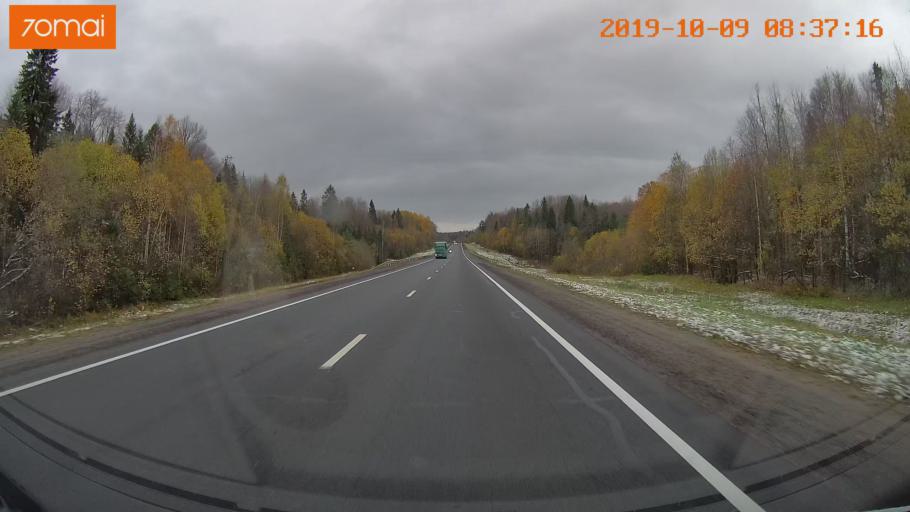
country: RU
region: Vologda
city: Gryazovets
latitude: 58.9387
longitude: 40.1751
